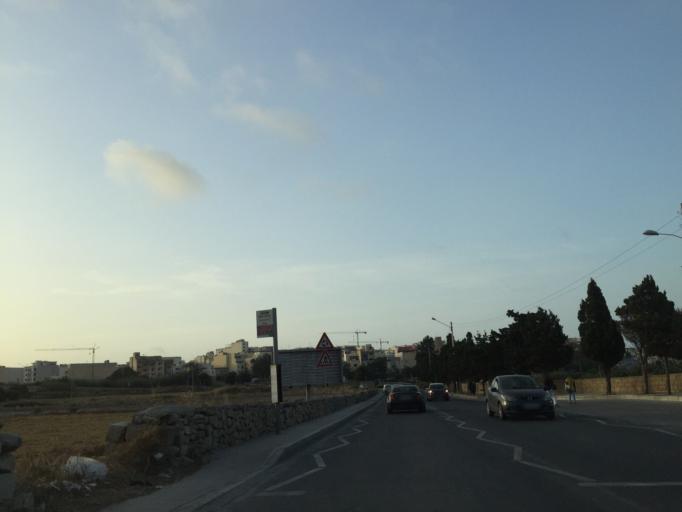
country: MT
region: Saint Paul's Bay
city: San Pawl il-Bahar
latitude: 35.9420
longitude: 14.4115
